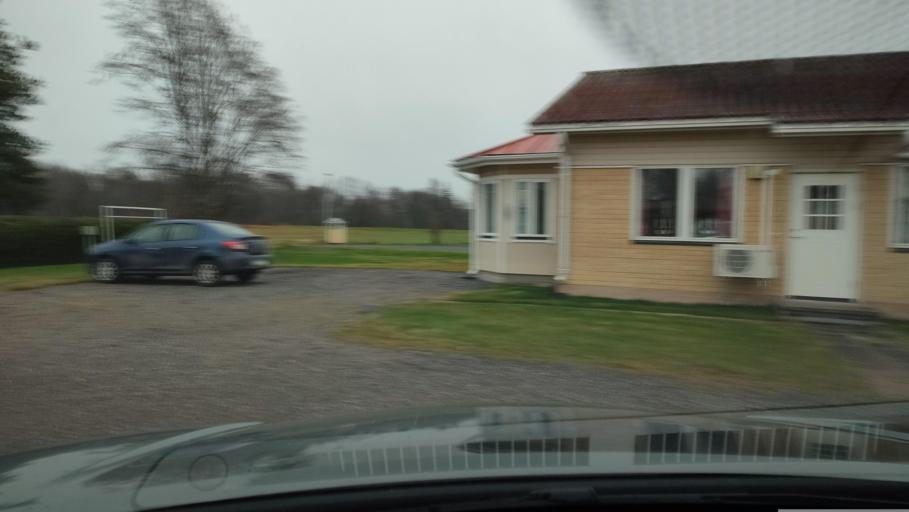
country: FI
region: Ostrobothnia
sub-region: Sydosterbotten
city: Kristinestad
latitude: 62.2536
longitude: 21.5049
